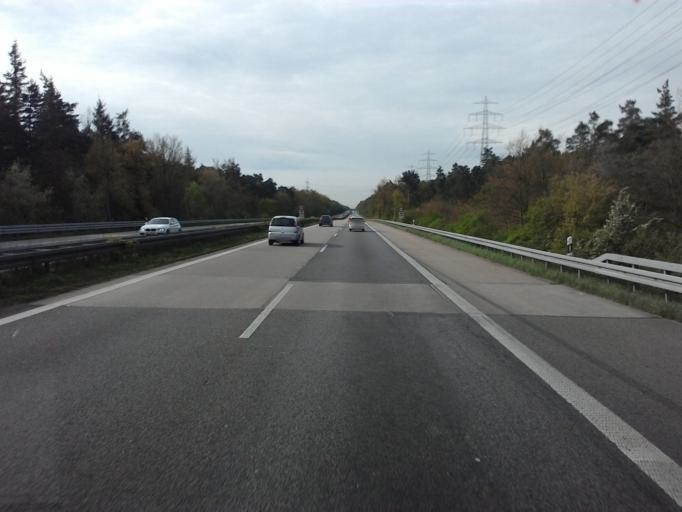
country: DE
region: Baden-Wuerttemberg
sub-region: Karlsruhe Region
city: Sandhausen
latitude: 49.3452
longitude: 8.6309
